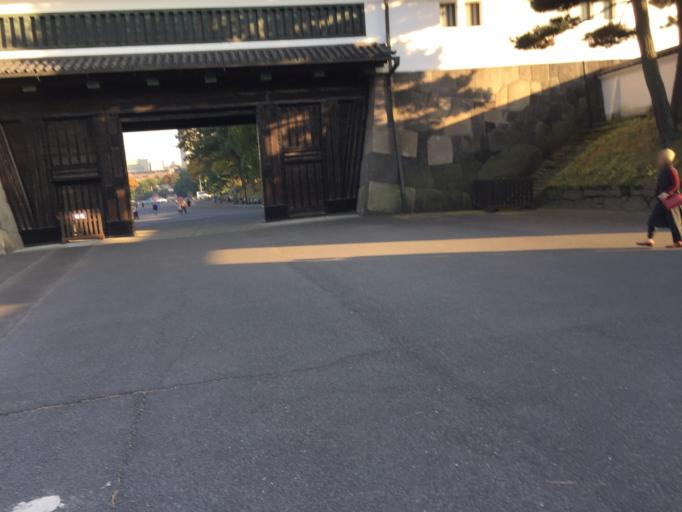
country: JP
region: Tokyo
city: Tokyo
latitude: 35.6786
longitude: 139.7537
